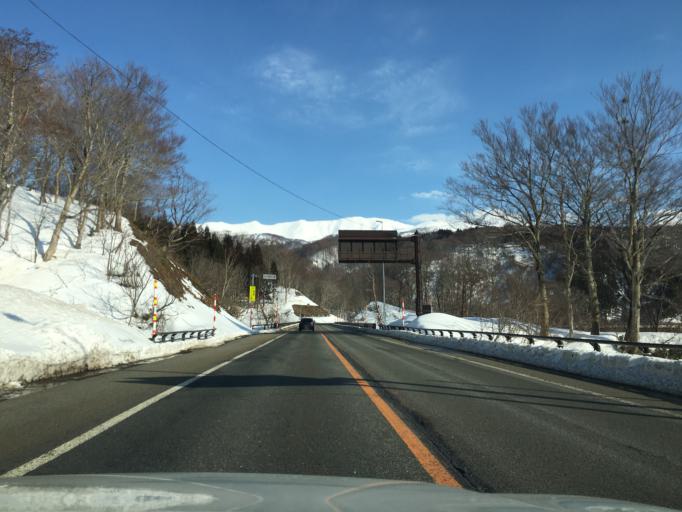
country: JP
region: Yamagata
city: Tsuruoka
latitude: 38.5807
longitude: 139.9400
